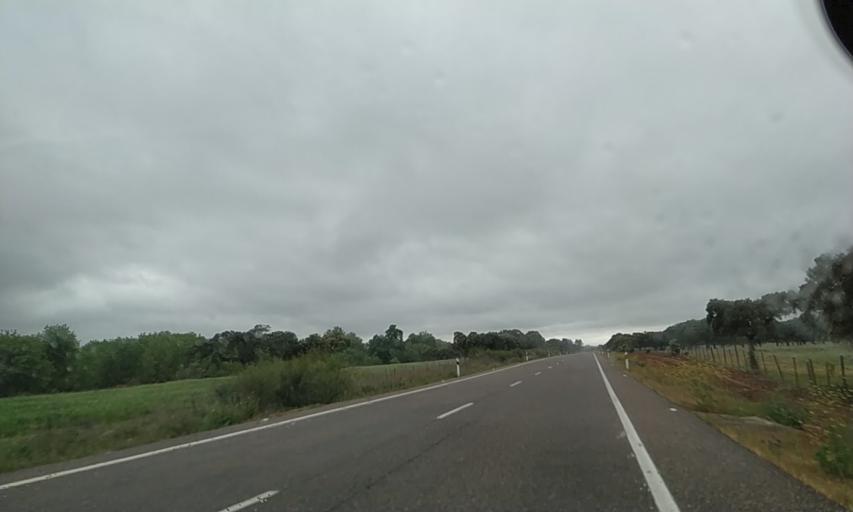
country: ES
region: Extremadura
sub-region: Provincia de Badajoz
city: La Roca de la Sierra
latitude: 39.0877
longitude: -6.7272
